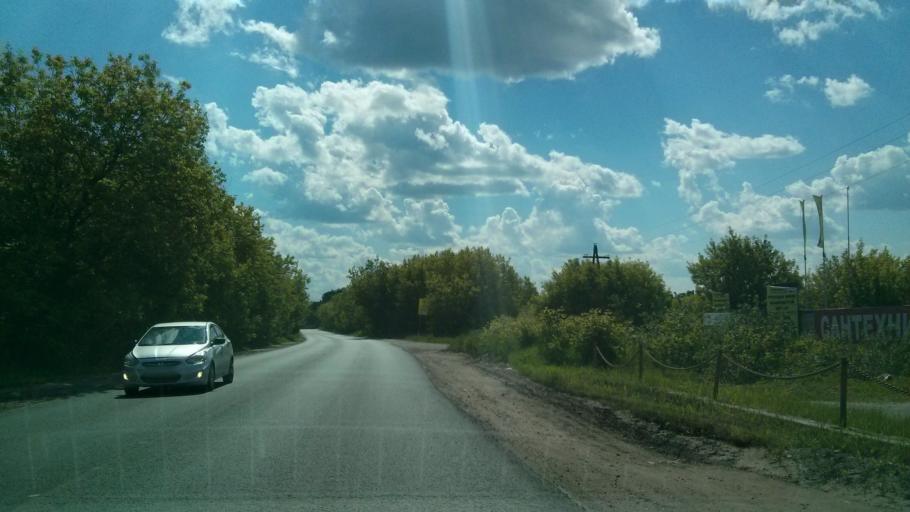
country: RU
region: Vladimir
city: Murom
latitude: 55.5530
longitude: 42.0041
